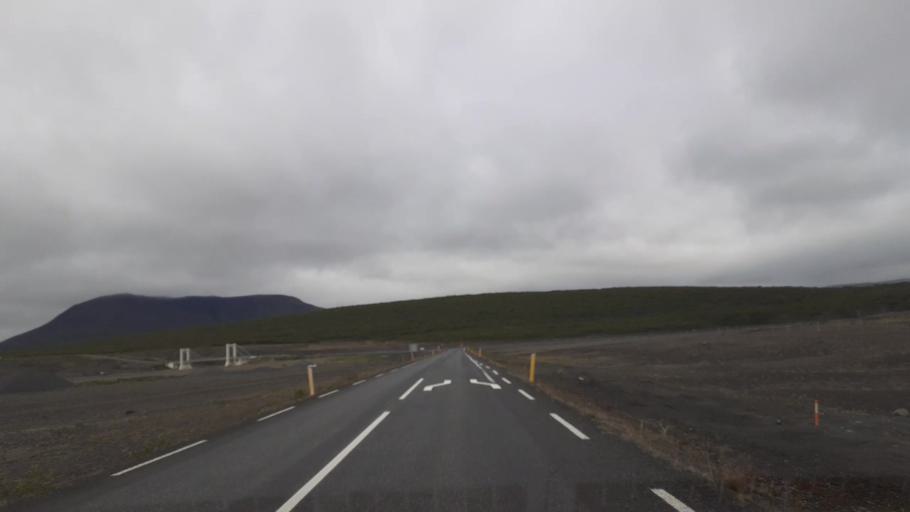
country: IS
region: Northeast
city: Husavik
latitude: 66.0308
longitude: -16.4563
